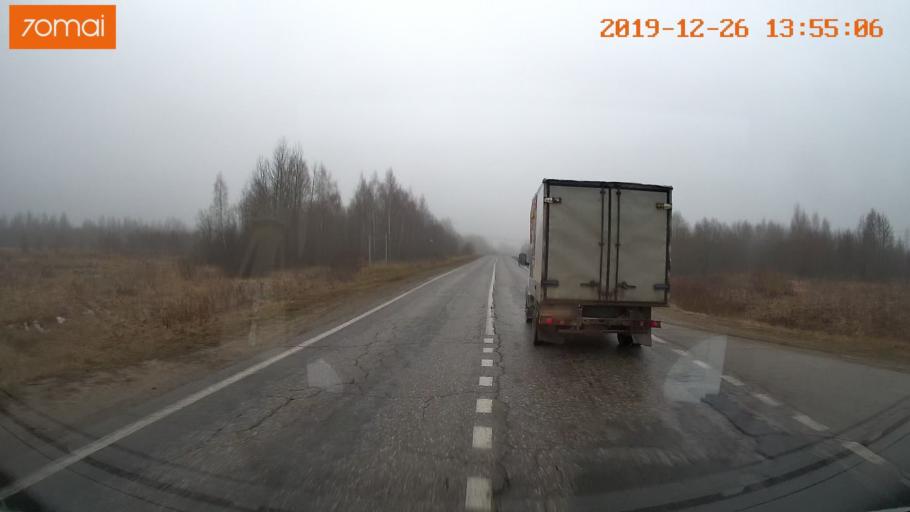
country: RU
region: Jaroslavl
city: Poshekhon'ye
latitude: 58.6069
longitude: 38.6432
